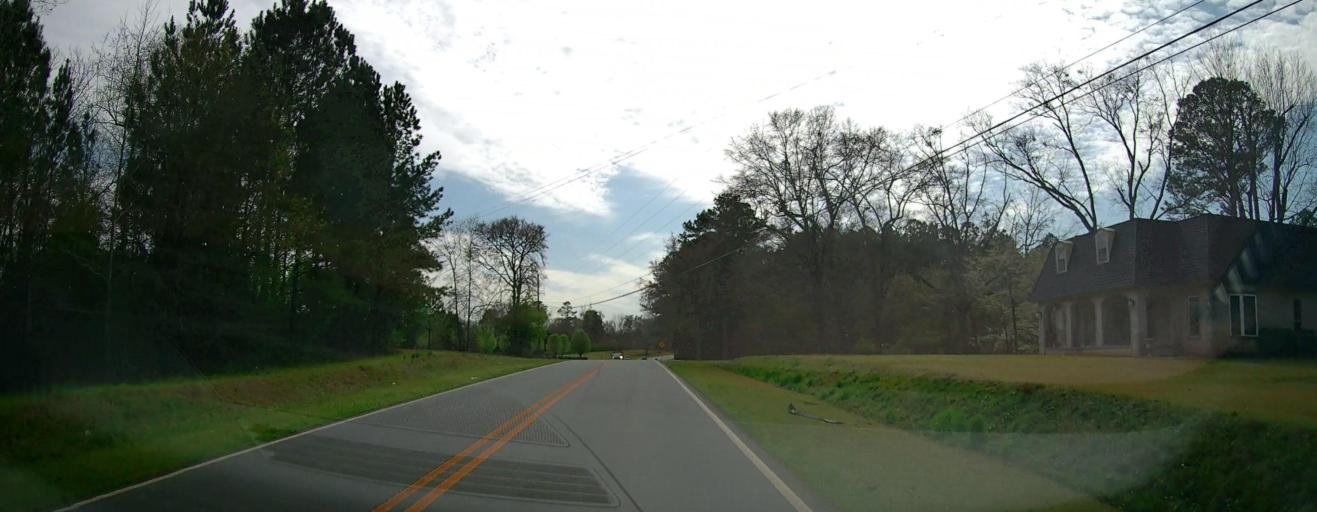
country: US
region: Georgia
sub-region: Monroe County
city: Forsyth
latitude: 33.0480
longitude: -83.8997
